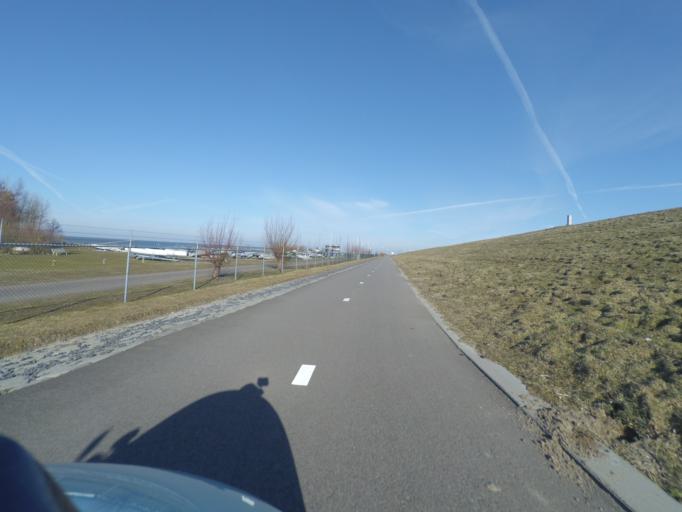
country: NL
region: North Holland
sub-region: Gemeente Naarden
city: Naarden
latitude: 52.3437
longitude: 5.1350
